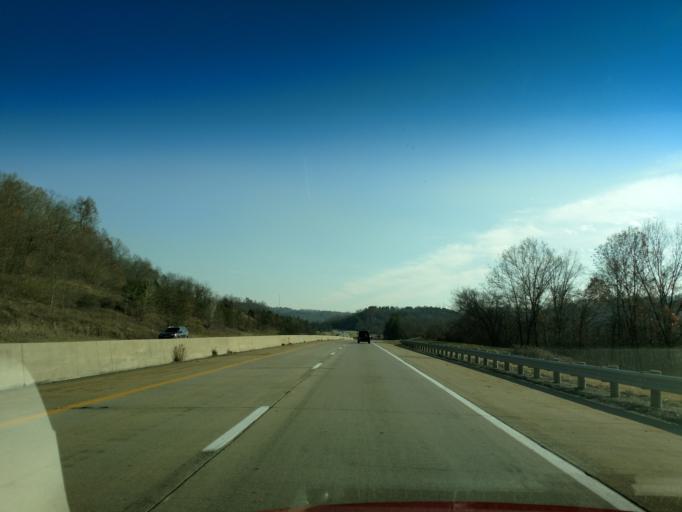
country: US
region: Ohio
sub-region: Noble County
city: Caldwell
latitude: 39.6745
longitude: -81.4859
